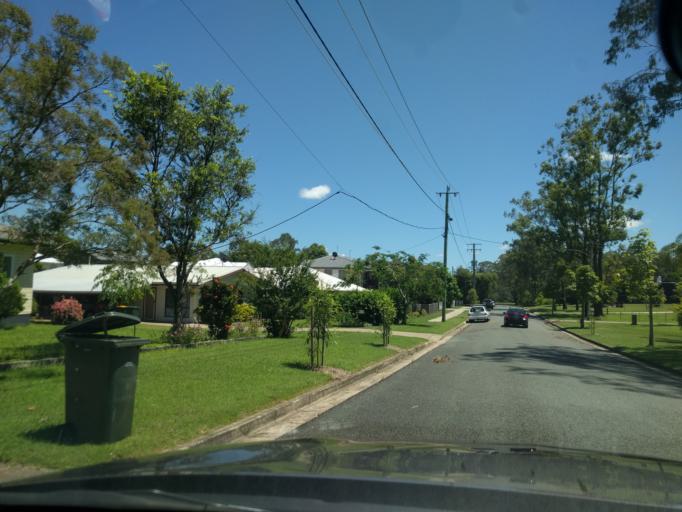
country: AU
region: Queensland
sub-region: Logan
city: Cedar Vale
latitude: -27.9875
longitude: 153.0071
